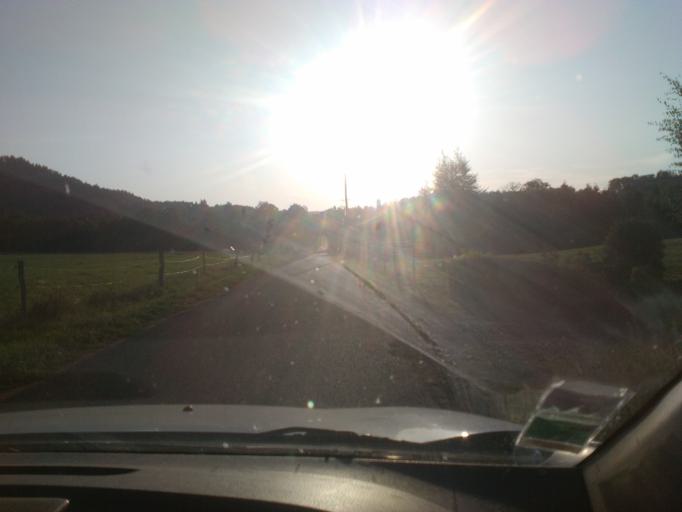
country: FR
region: Lorraine
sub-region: Departement des Vosges
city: Saint-Michel-sur-Meurthe
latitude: 48.3215
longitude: 6.8663
